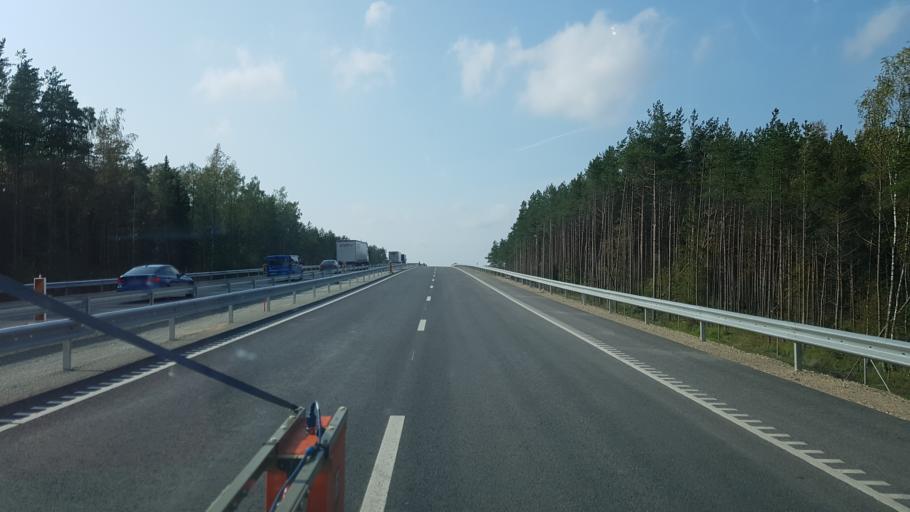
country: EE
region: Harju
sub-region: Saku vald
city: Saku
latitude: 59.3118
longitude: 24.7268
